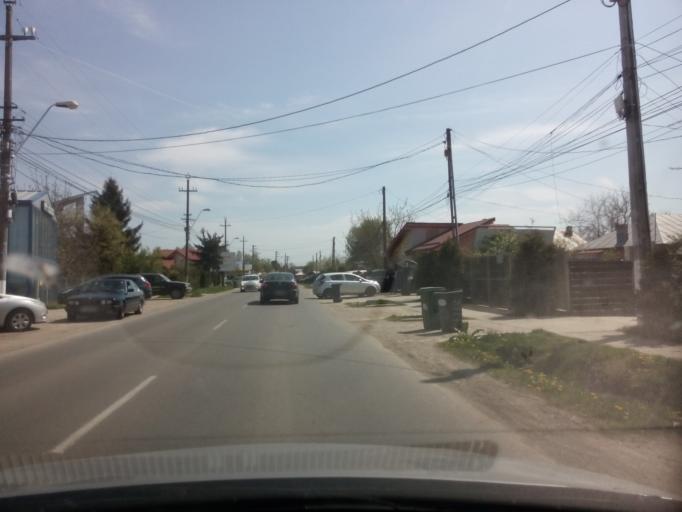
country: RO
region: Ilfov
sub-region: Comuna Corbeanca
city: Corbeanca
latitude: 44.5941
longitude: 26.0392
